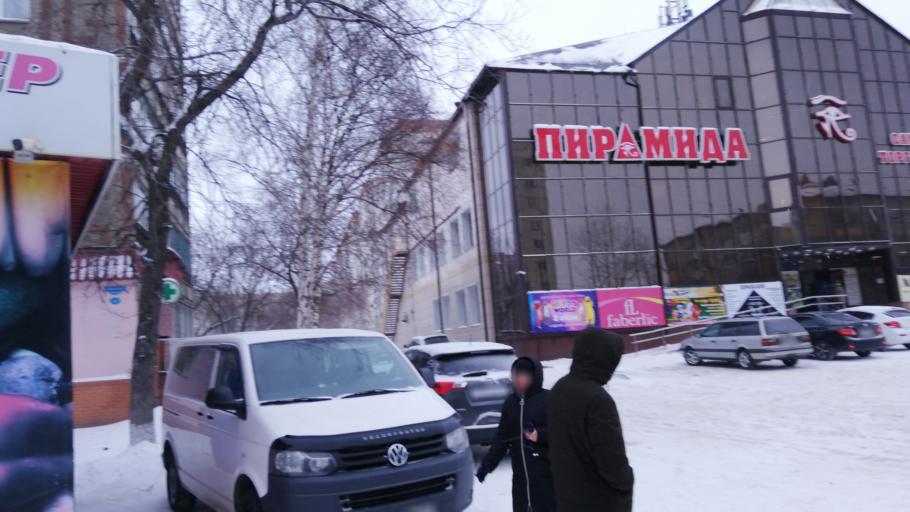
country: KZ
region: Soltustik Qazaqstan
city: Petropavlovsk
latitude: 54.8604
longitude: 69.1660
